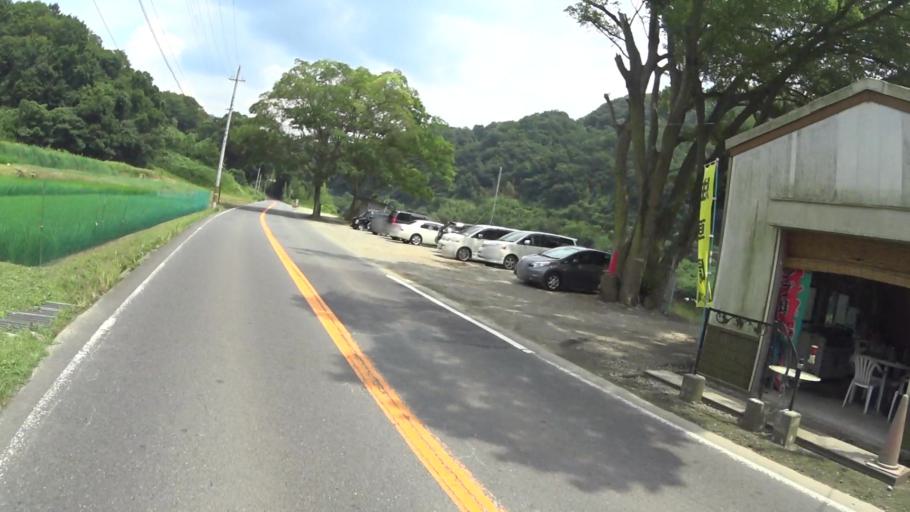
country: JP
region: Nara
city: Nara-shi
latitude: 34.7630
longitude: 135.8953
